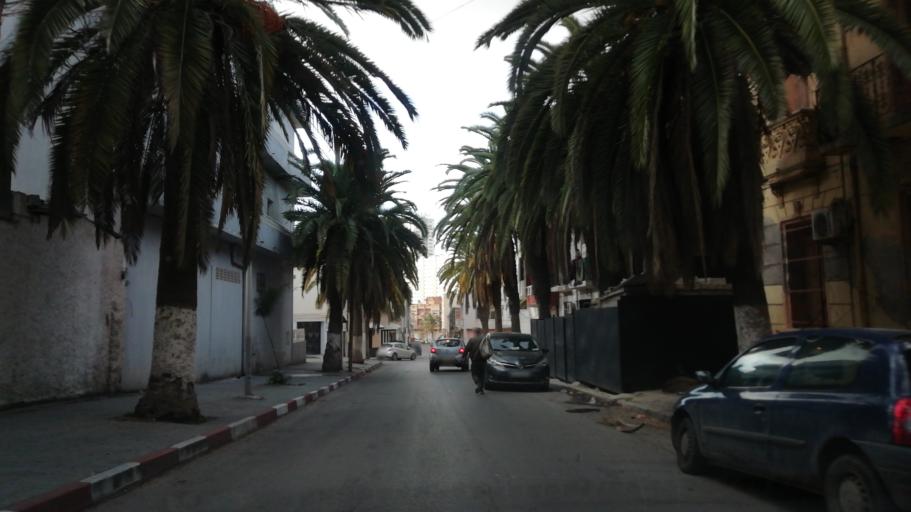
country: DZ
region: Oran
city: Oran
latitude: 35.7115
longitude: -0.6151
